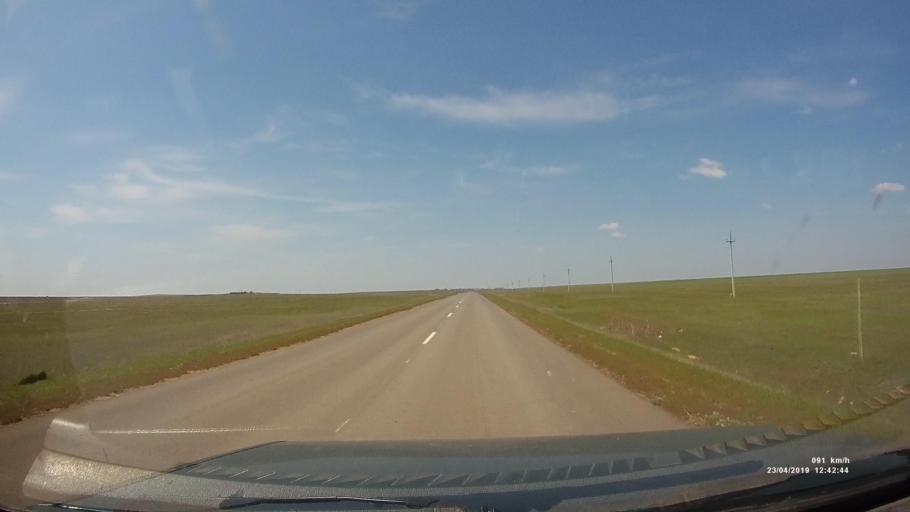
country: RU
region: Kalmykiya
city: Yashalta
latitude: 46.4582
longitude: 42.6609
